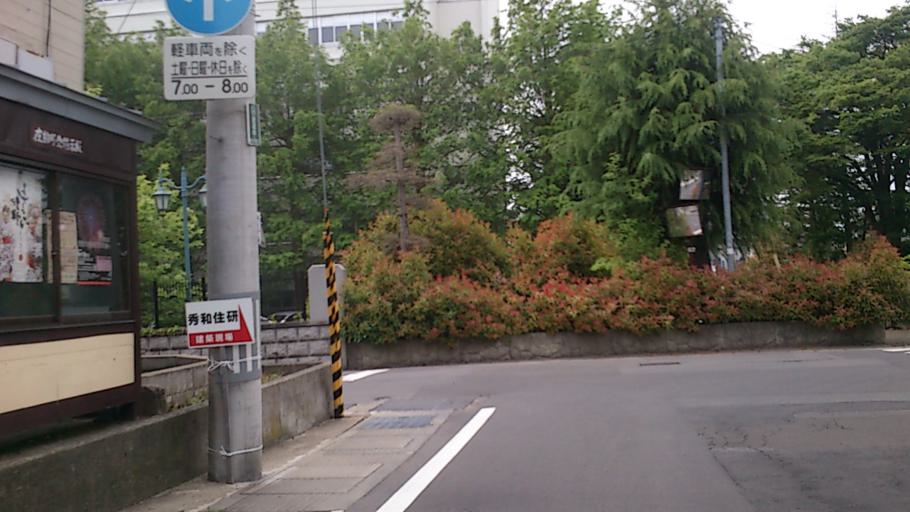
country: JP
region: Aomori
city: Hirosaki
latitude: 40.5996
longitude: 140.4638
